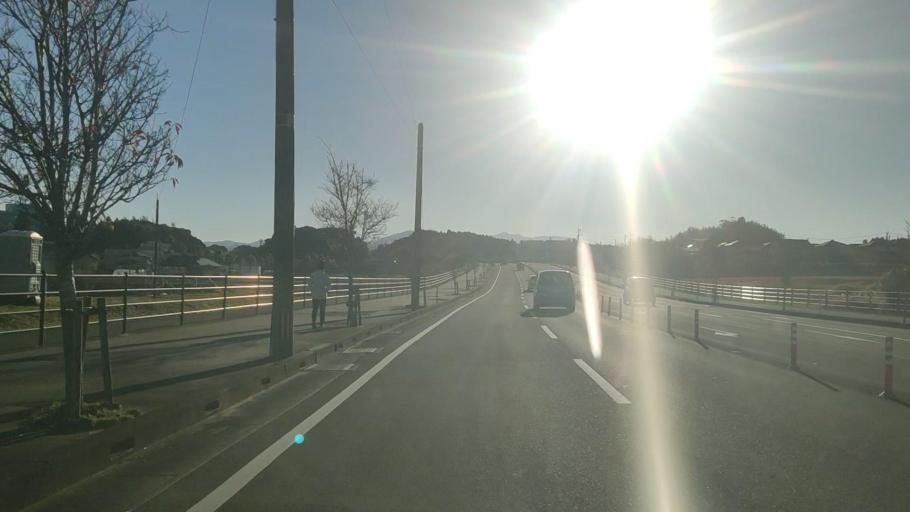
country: JP
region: Miyazaki
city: Miyazaki-shi
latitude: 31.8920
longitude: 131.4056
